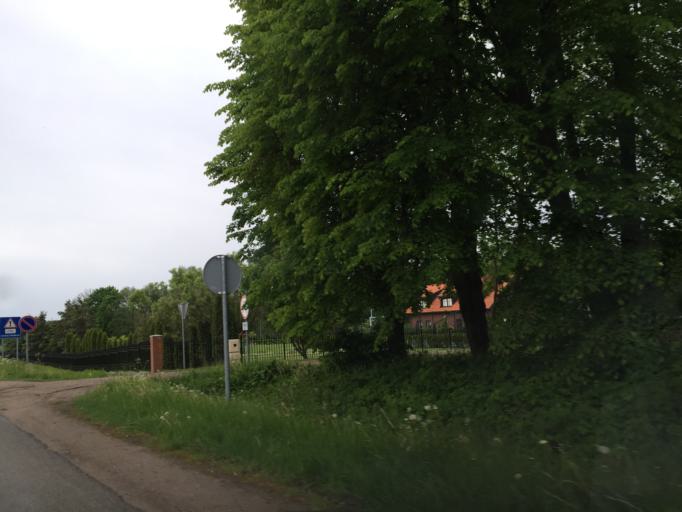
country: LT
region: Klaipedos apskritis
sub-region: Klaipeda
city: Klaipeda
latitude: 55.8059
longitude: 21.0755
